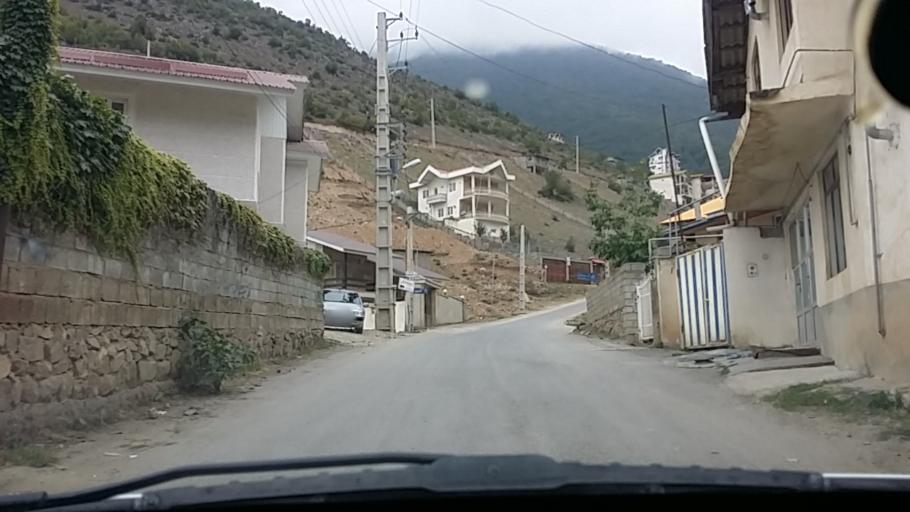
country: IR
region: Mazandaran
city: `Abbasabad
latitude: 36.4786
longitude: 51.1391
